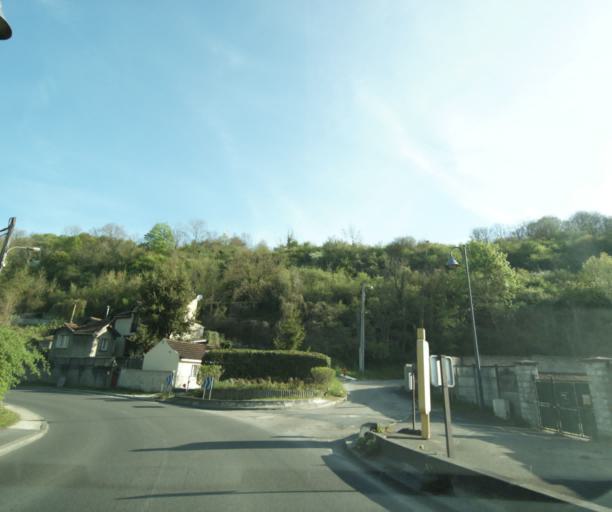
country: FR
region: Ile-de-France
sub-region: Departement de Seine-et-Marne
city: Moret-sur-Loing
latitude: 48.3772
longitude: 2.8205
